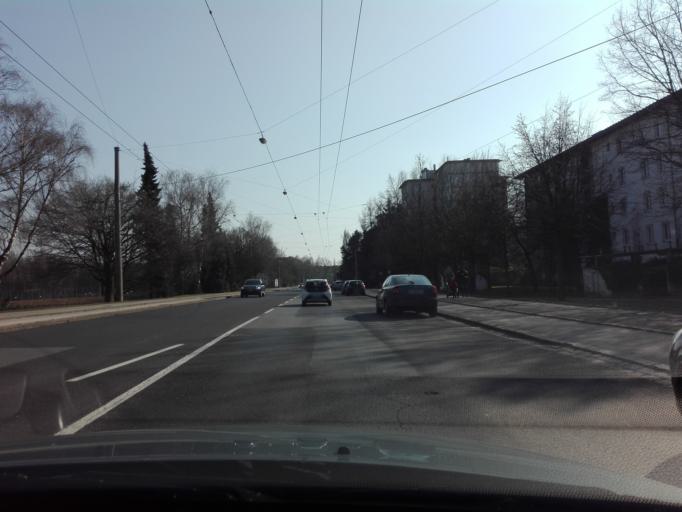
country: AT
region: Upper Austria
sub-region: Politischer Bezirk Linz-Land
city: Leonding
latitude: 48.2616
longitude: 14.2900
